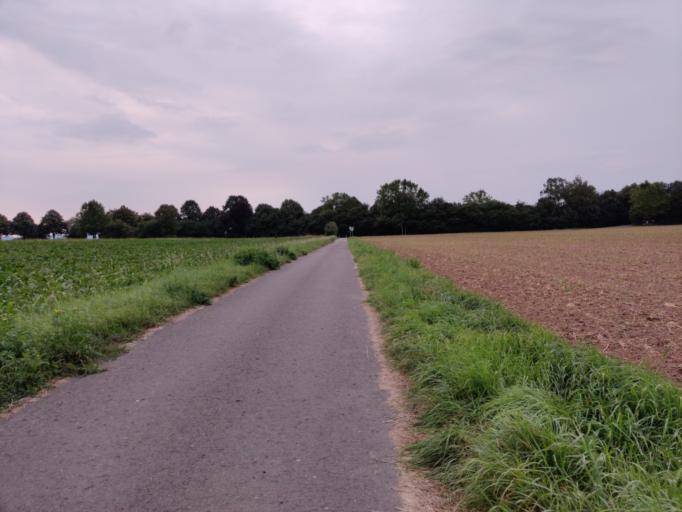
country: DE
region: Lower Saxony
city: Hameln
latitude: 52.0664
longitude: 9.3580
